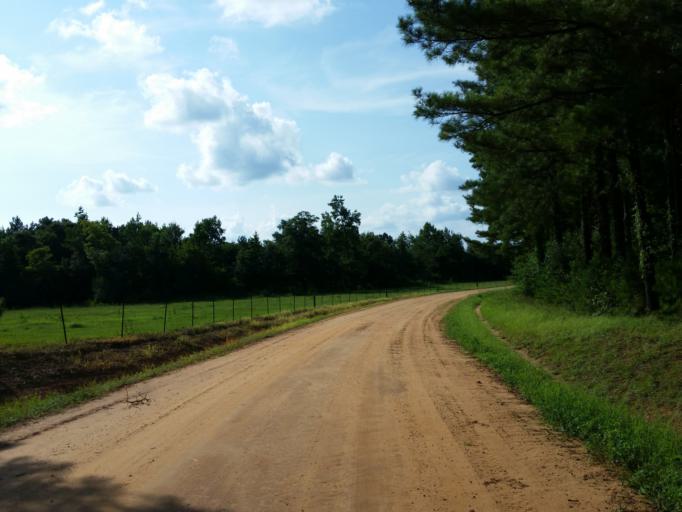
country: US
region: Georgia
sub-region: Lee County
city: Leesburg
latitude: 31.8799
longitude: -84.0423
